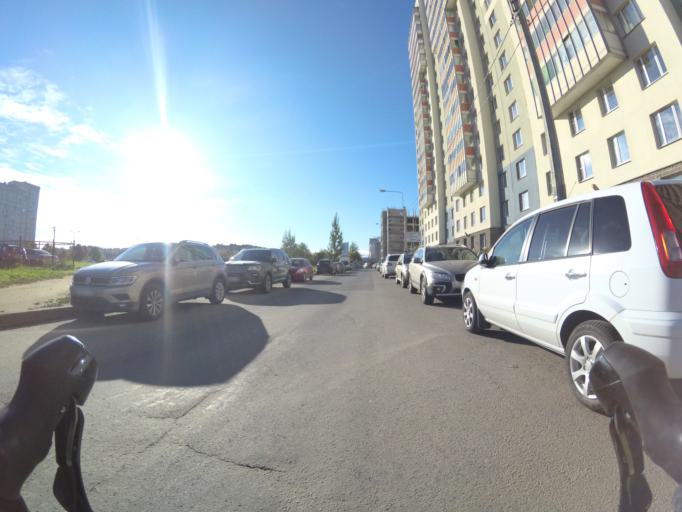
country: RU
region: Leningrad
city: Untolovo
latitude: 59.9972
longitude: 30.2063
